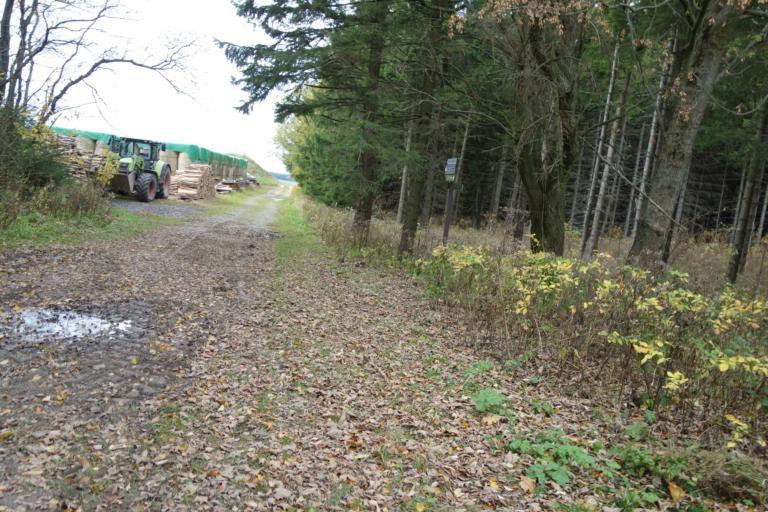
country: CZ
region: Ustecky
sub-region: Okres Chomutov
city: Vejprty
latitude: 50.4722
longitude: 12.9871
